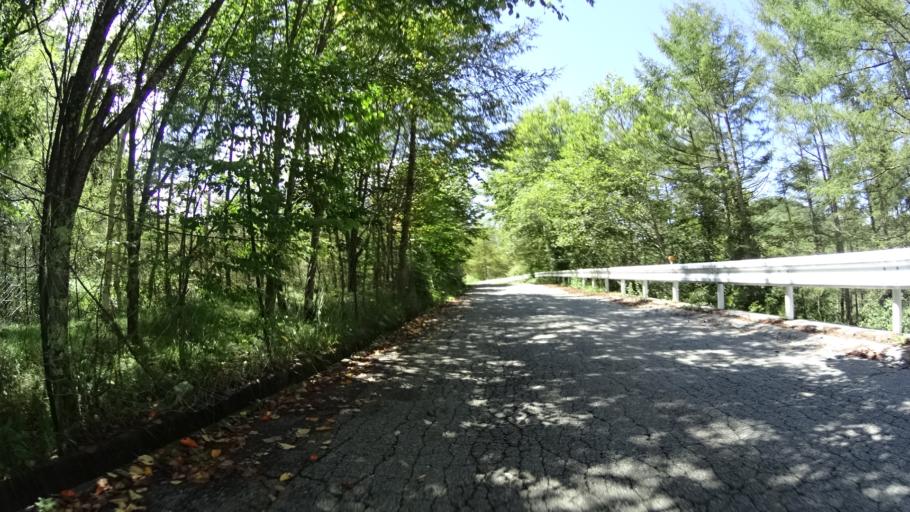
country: JP
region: Yamanashi
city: Enzan
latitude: 35.7243
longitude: 138.8423
